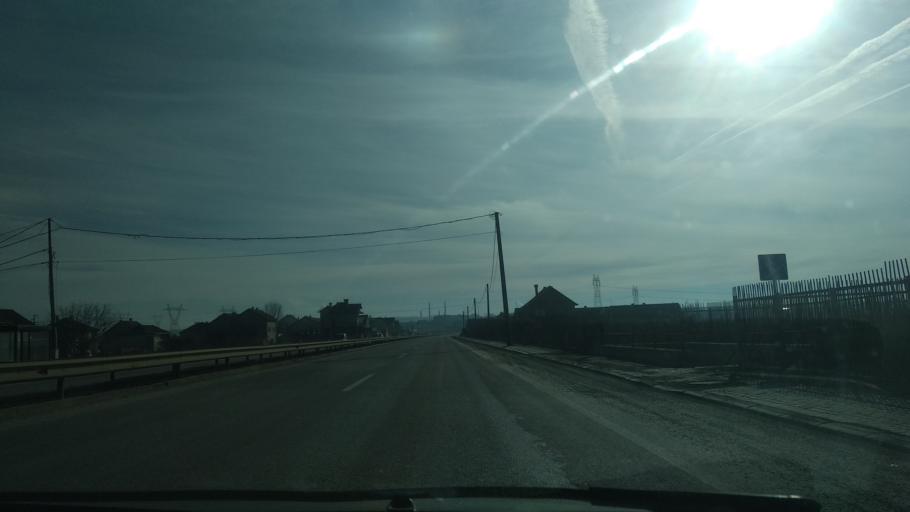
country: XK
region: Pristina
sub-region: Komuna e Obiliqit
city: Obiliq
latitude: 42.7092
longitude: 21.1030
